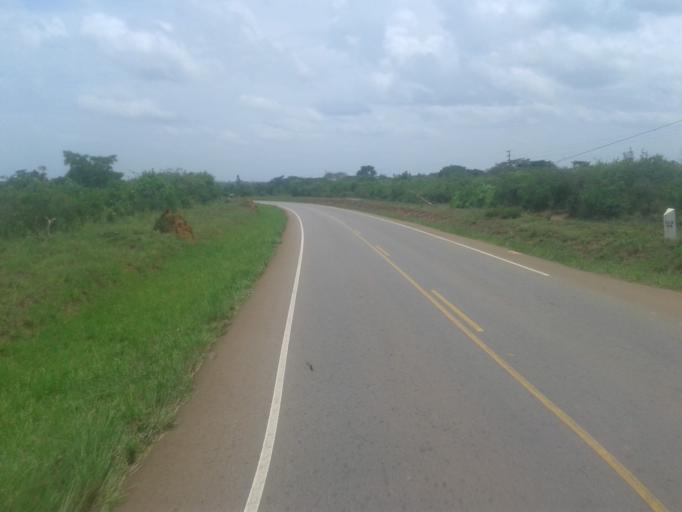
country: UG
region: Central Region
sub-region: Nakasongola District
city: Nakasongola
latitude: 1.3971
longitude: 32.3145
